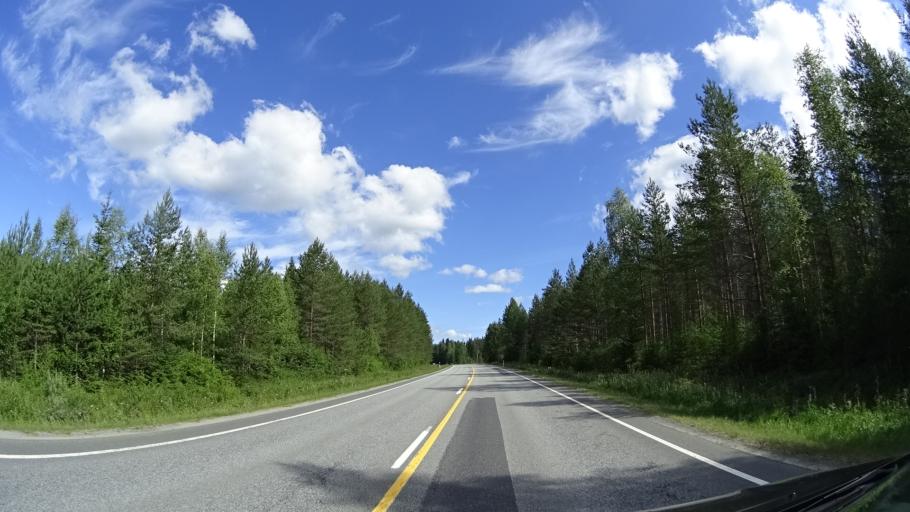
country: FI
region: Pirkanmaa
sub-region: Luoteis-Pirkanmaa
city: Kihnioe
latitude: 62.1778
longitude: 23.1718
